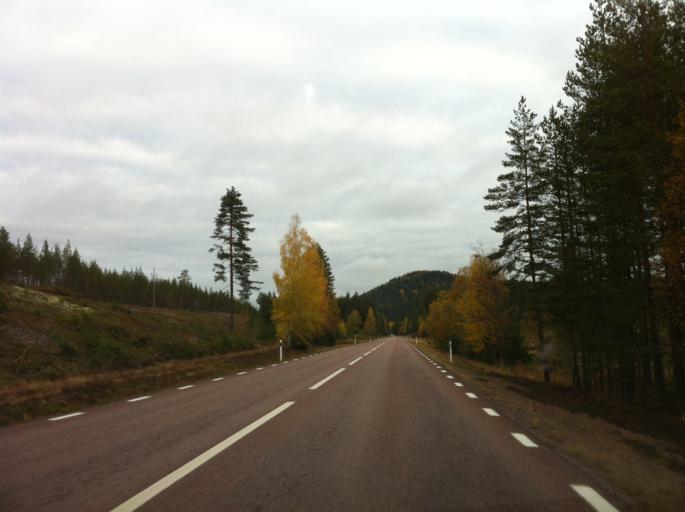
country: SE
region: Dalarna
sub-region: Mora Kommun
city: Mora
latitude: 61.0772
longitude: 14.3413
